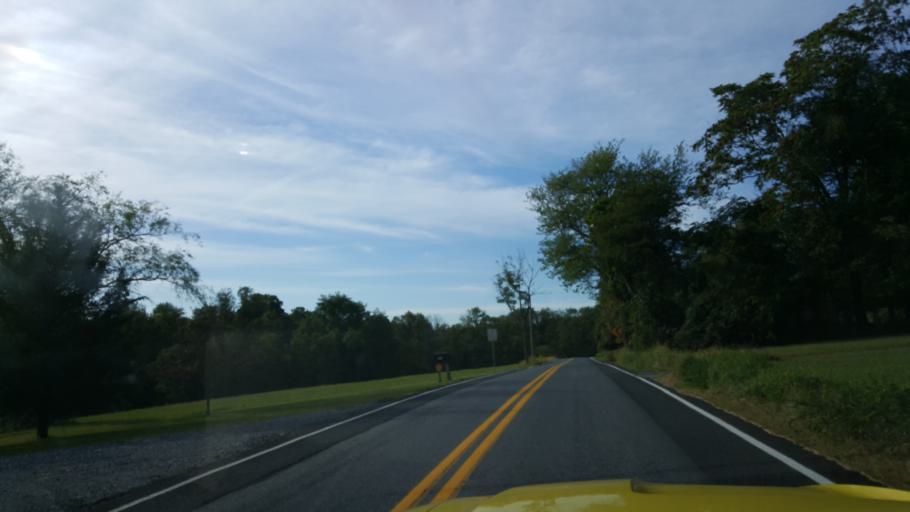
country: US
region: Pennsylvania
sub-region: Lebanon County
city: Campbelltown
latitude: 40.2452
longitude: -76.5652
